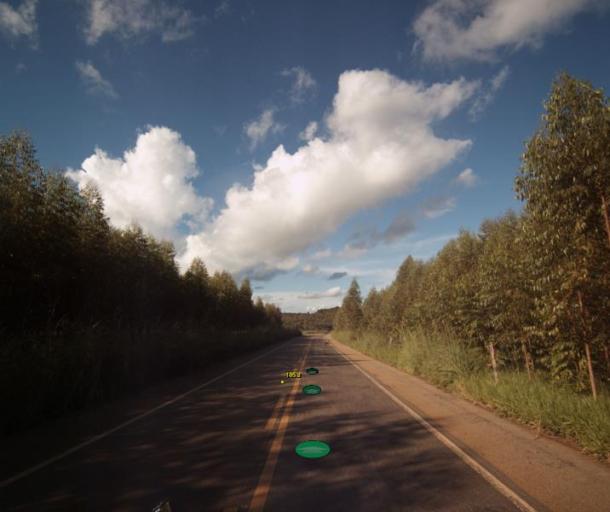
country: BR
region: Goias
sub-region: Itaberai
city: Itaberai
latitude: -16.0023
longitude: -49.7522
